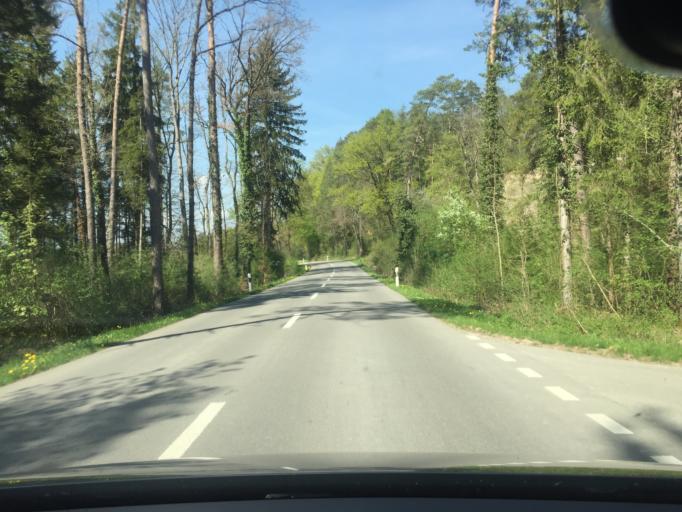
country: DE
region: Baden-Wuerttemberg
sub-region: Freiburg Region
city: Lottstetten
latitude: 47.5979
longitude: 8.6064
